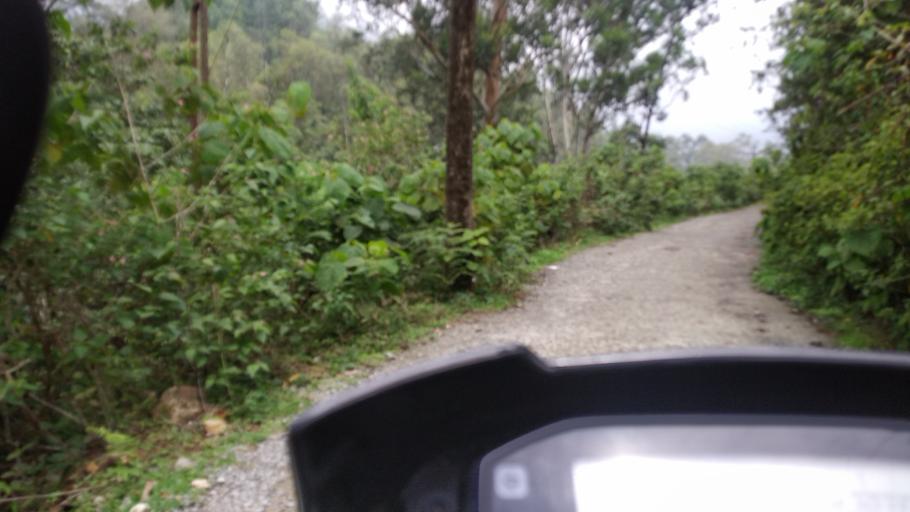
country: IN
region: Kerala
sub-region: Kottayam
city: Erattupetta
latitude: 9.6103
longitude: 76.9707
